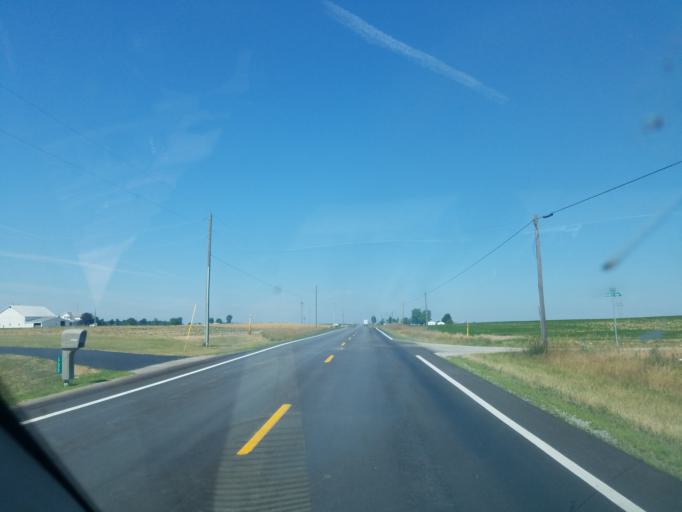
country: US
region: Ohio
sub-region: Shelby County
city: Jackson Center
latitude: 40.4394
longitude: -84.1068
